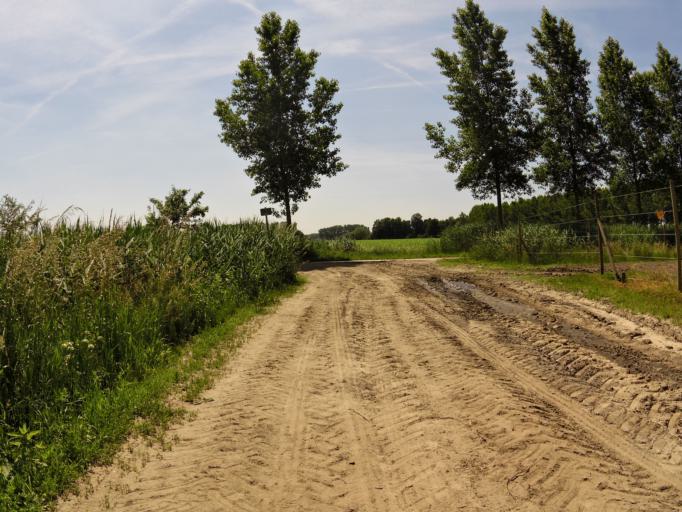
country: NL
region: North Brabant
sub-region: Gemeente Schijndel
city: Schijndel
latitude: 51.5799
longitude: 5.3969
